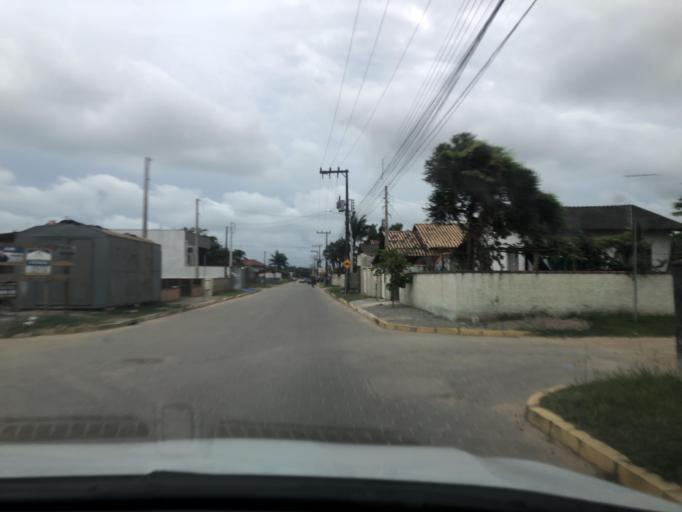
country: BR
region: Santa Catarina
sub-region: Sao Francisco Do Sul
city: Sao Francisco do Sul
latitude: -26.2313
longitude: -48.5244
